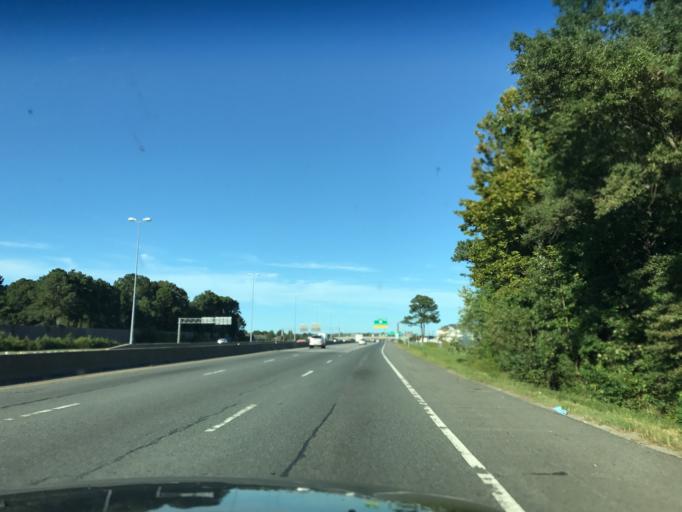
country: US
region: Virginia
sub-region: City of Chesapeake
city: Chesapeake
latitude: 36.7669
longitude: -76.2626
